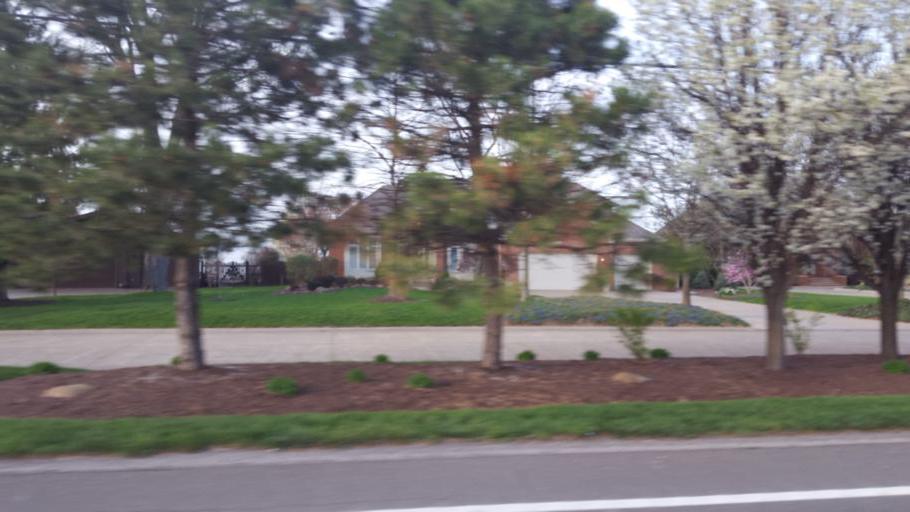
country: US
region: Ohio
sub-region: Erie County
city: Huron
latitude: 41.3856
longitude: -82.5218
